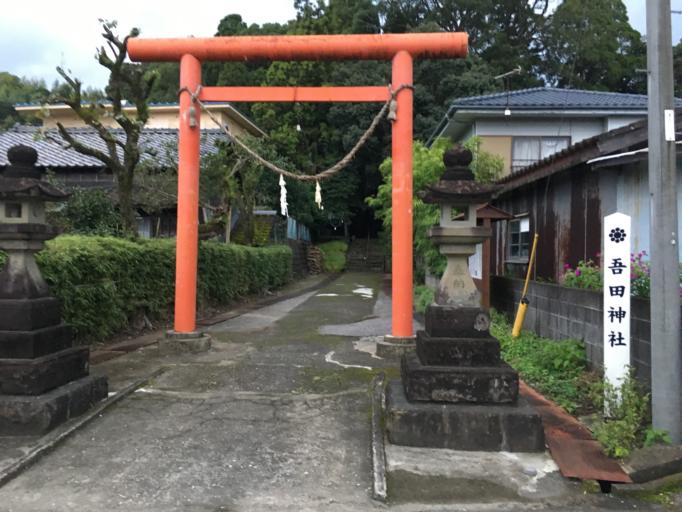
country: JP
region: Miyazaki
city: Nichinan
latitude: 31.6016
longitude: 131.3768
